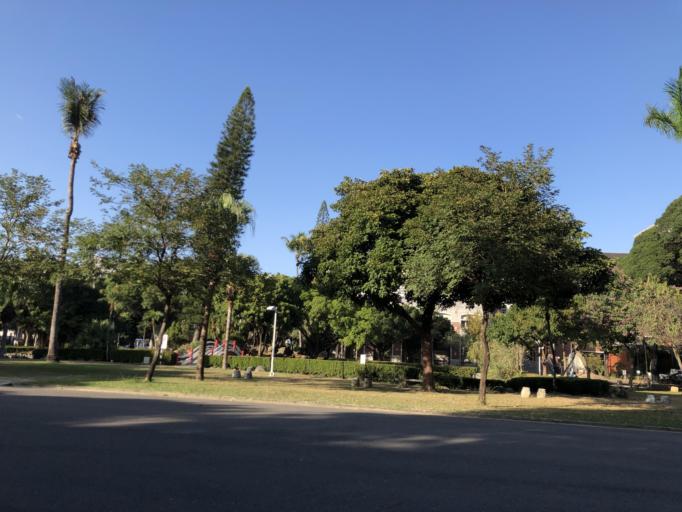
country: TW
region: Taiwan
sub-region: Tainan
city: Tainan
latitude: 22.9997
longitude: 120.2174
